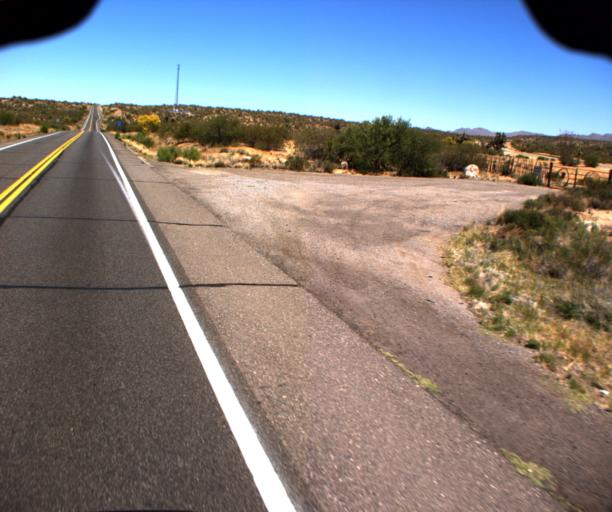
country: US
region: Arizona
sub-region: Yavapai County
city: Congress
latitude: 34.2087
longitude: -113.0650
